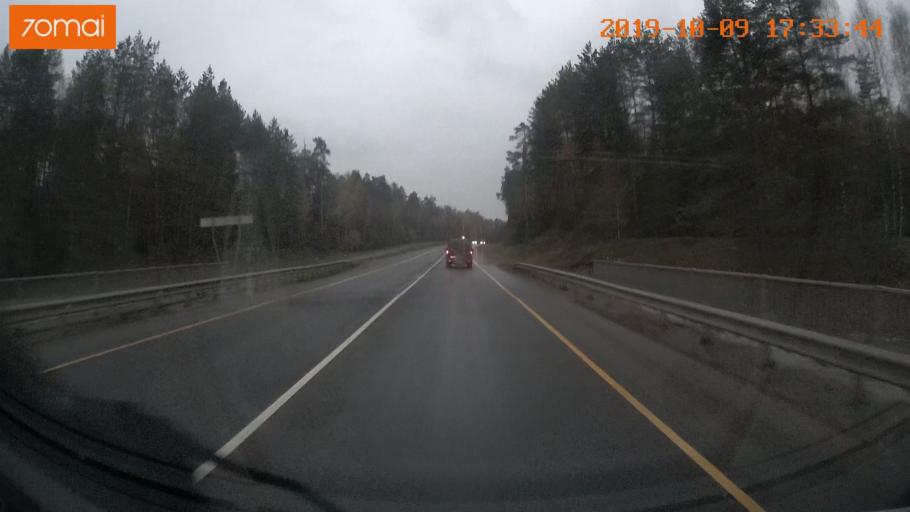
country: RU
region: Ivanovo
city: Bogorodskoye
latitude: 57.1142
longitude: 41.0179
